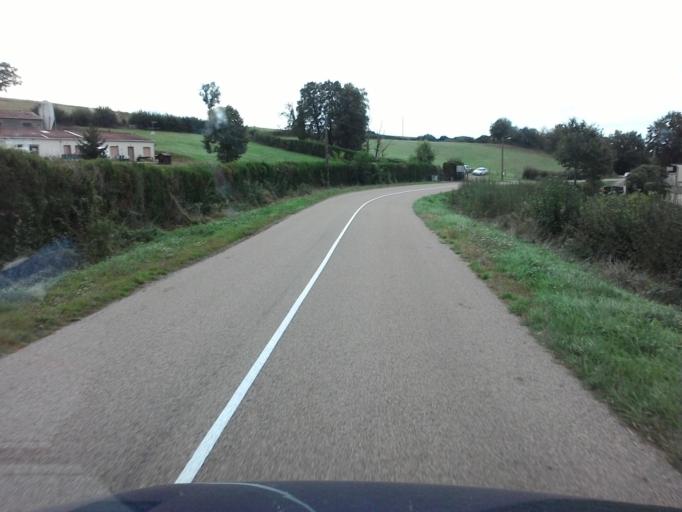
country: FR
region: Bourgogne
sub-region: Departement de Saone-et-Loire
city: Montcenis
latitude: 46.7736
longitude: 4.3740
